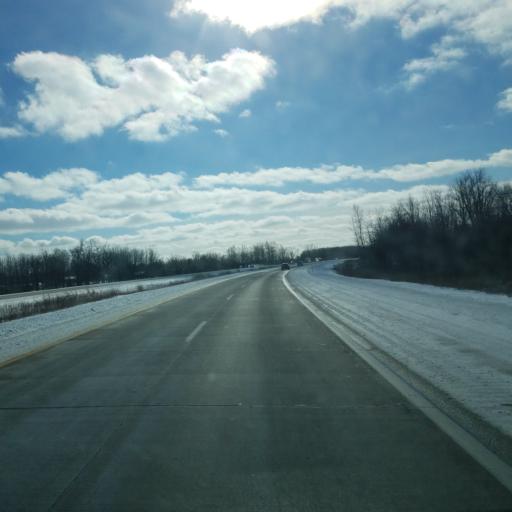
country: US
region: Michigan
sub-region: Clinton County
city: DeWitt
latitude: 42.8830
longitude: -84.5157
